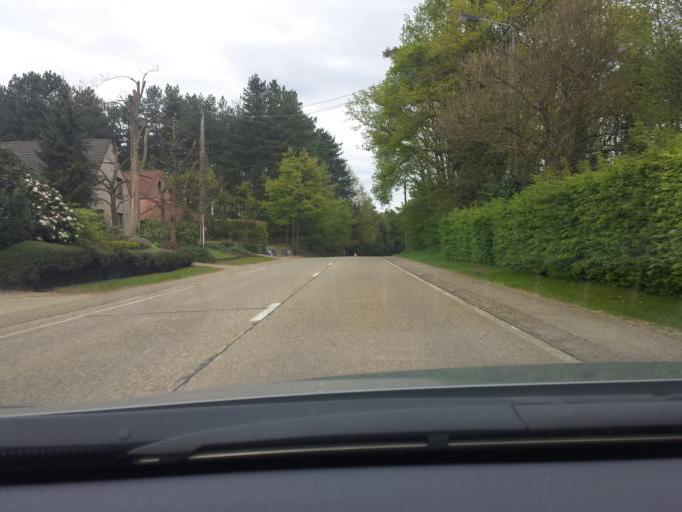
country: BE
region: Flanders
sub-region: Provincie Limburg
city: Lummen
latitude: 50.9897
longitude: 5.2076
